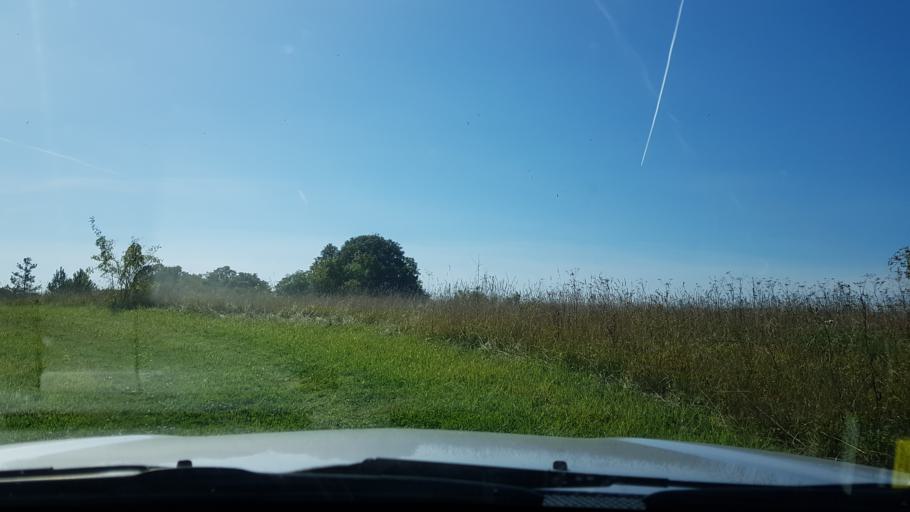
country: EE
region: Ida-Virumaa
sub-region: Sillamaee linn
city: Sillamae
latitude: 59.3913
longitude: 27.8095
